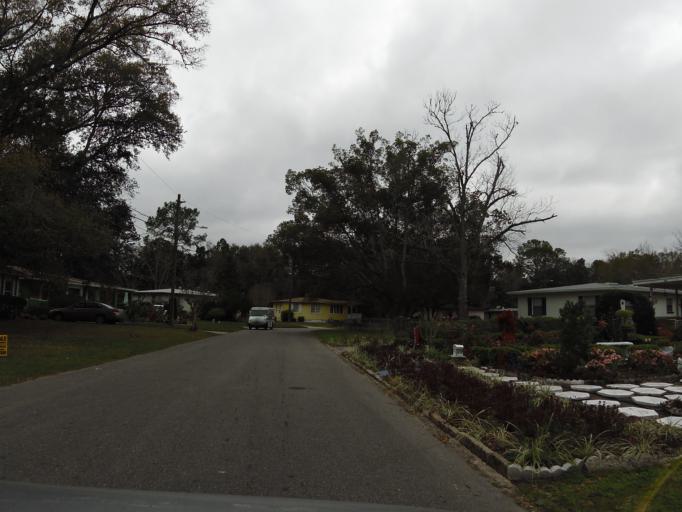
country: US
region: Florida
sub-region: Duval County
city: Jacksonville
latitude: 30.3732
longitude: -81.7059
